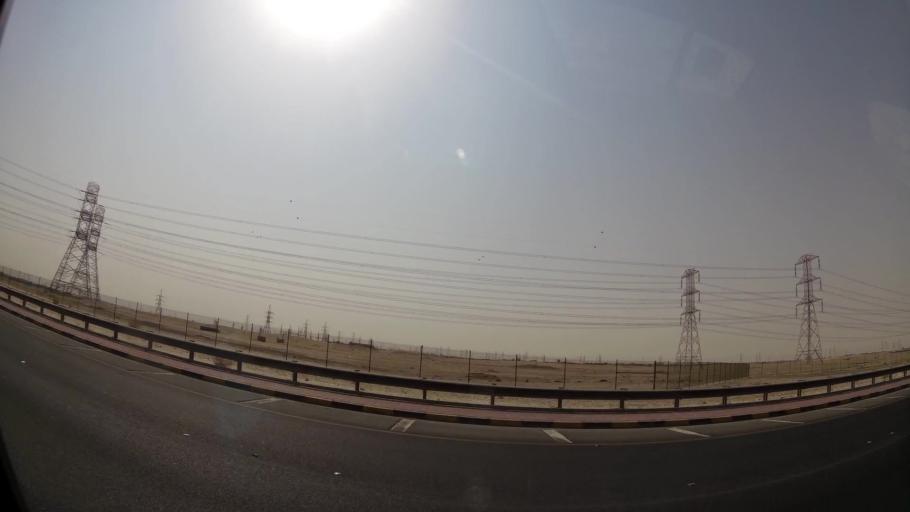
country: KW
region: Muhafazat al Jahra'
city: Al Jahra'
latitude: 29.2975
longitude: 47.7215
